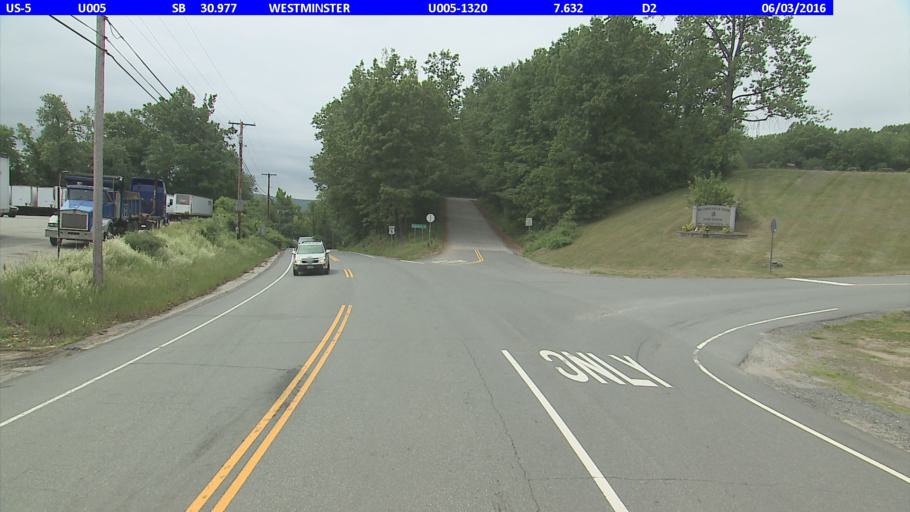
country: US
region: Vermont
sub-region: Windham County
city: Bellows Falls
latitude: 43.1181
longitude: -72.4371
